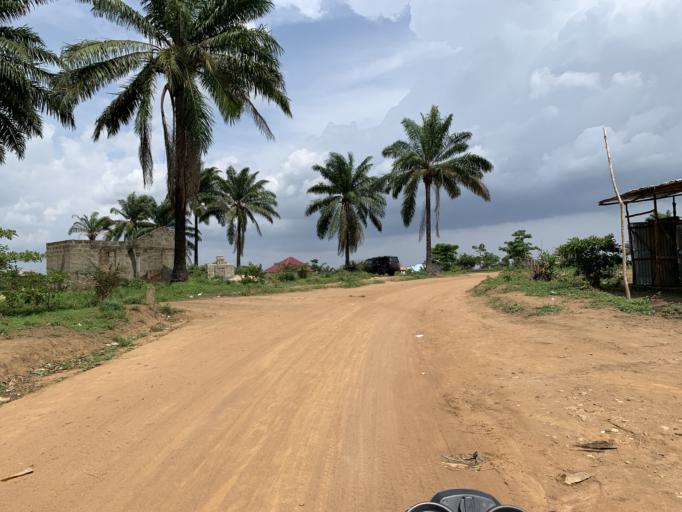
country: SL
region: Western Area
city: Waterloo
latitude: 8.3602
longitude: -13.0448
